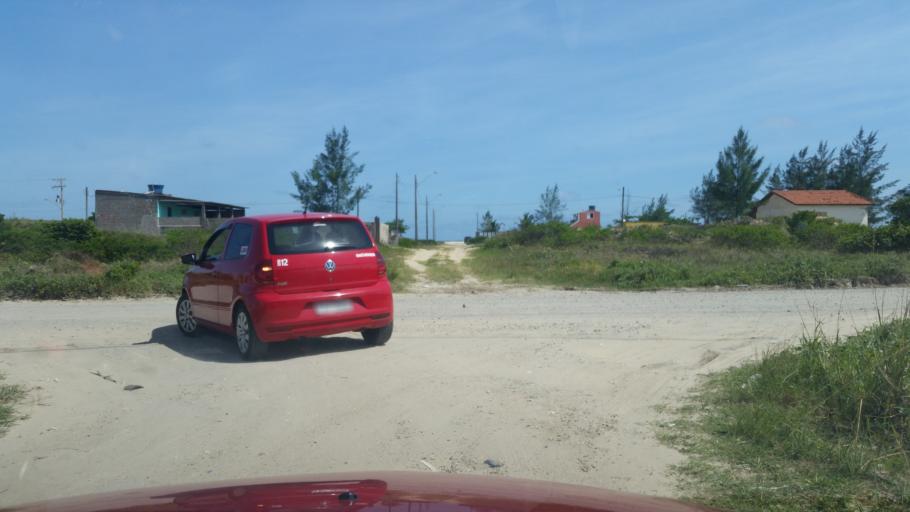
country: BR
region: Sao Paulo
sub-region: Iguape
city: Iguape
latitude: -24.7011
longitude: -47.4630
